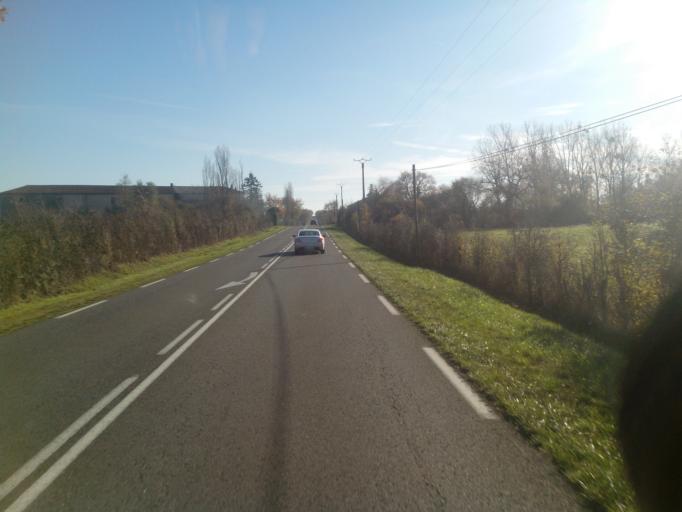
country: FR
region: Poitou-Charentes
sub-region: Departement de la Vienne
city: Lussac-les-Chateaux
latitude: 46.3661
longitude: 0.7691
